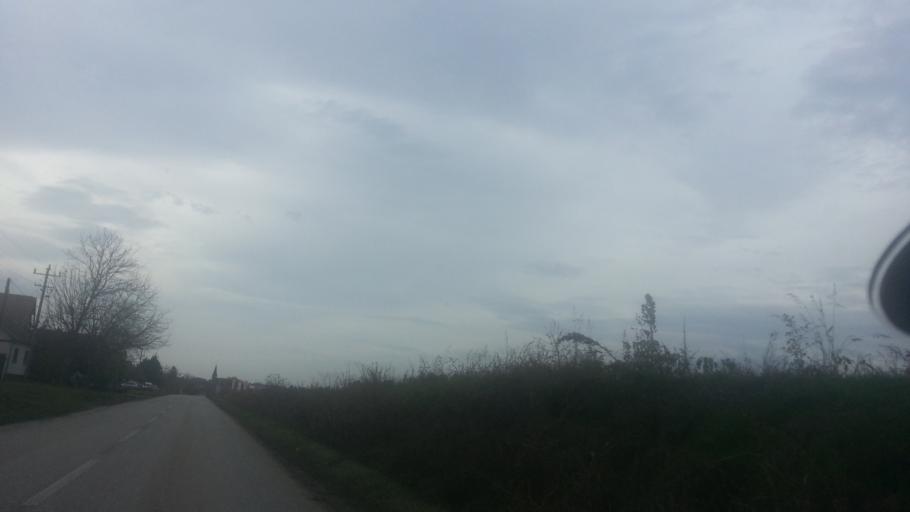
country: RS
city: Putinci
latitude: 44.9912
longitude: 19.9872
